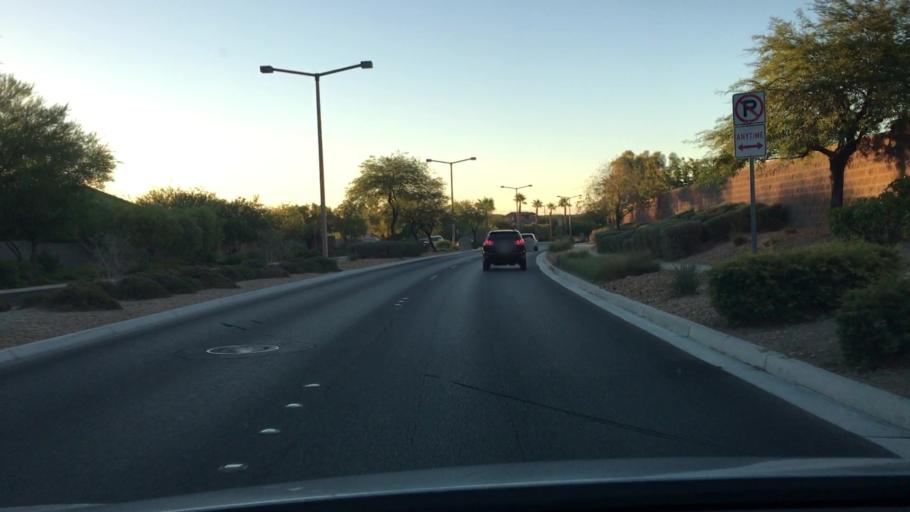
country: US
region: Nevada
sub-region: Clark County
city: Summerlin South
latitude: 36.1547
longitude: -115.3458
